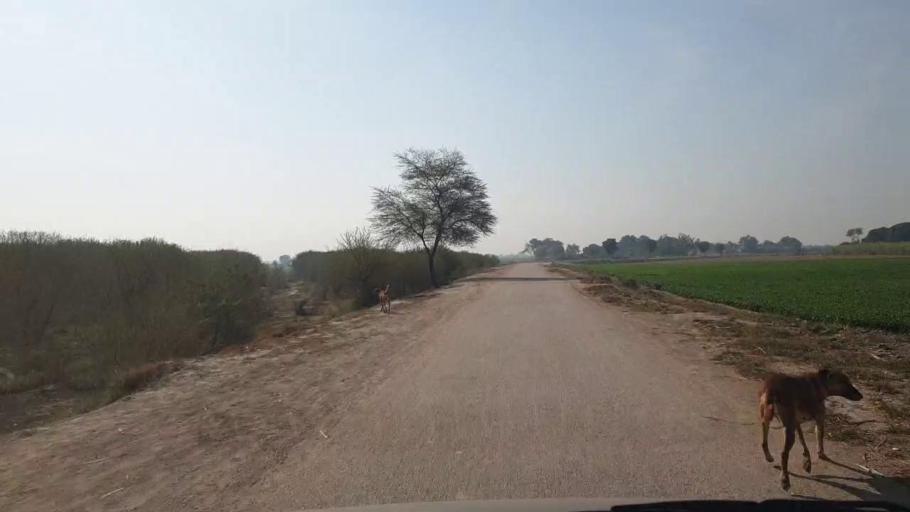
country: PK
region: Sindh
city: Tando Allahyar
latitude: 25.4154
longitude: 68.7437
